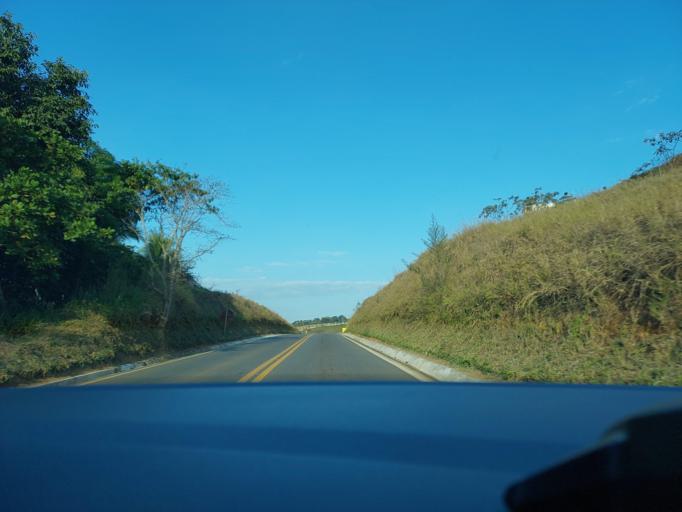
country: BR
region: Minas Gerais
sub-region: Muriae
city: Muriae
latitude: -21.1114
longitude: -42.4485
